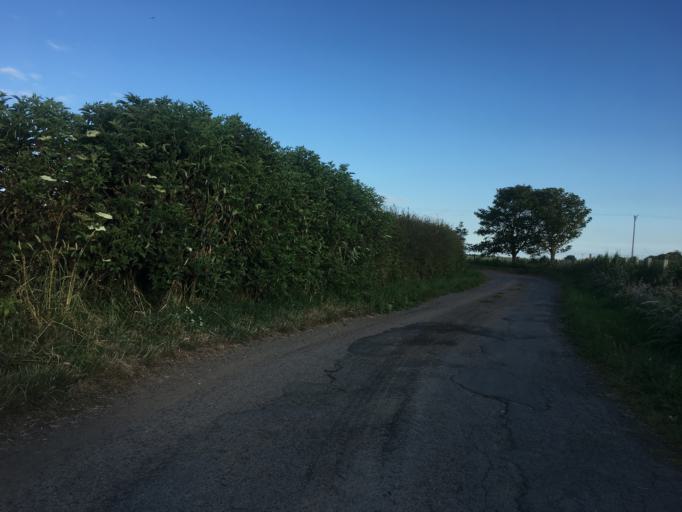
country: GB
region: England
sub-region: Northumberland
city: Bamburgh
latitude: 55.5921
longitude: -1.6945
